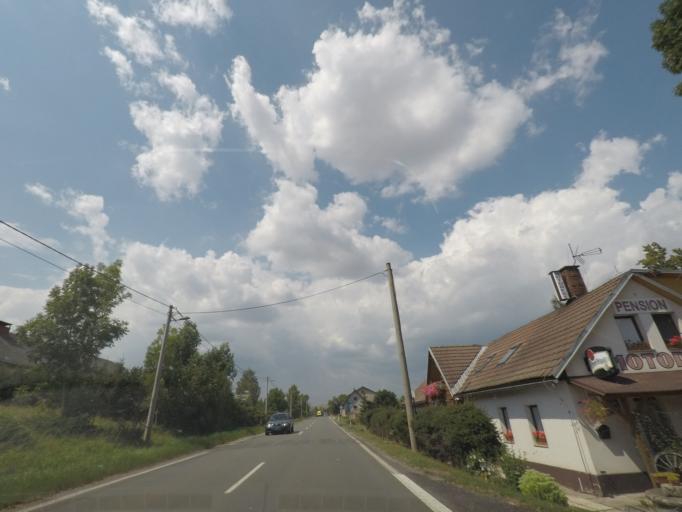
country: CZ
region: Kralovehradecky
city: Zadni Mostek
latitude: 50.5394
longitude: 15.6517
